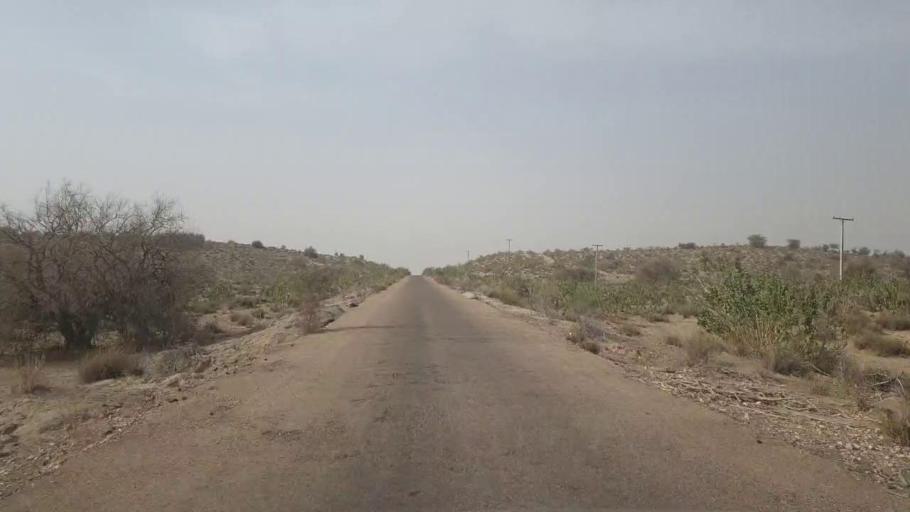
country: PK
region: Sindh
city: Chor
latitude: 25.6107
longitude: 69.9334
